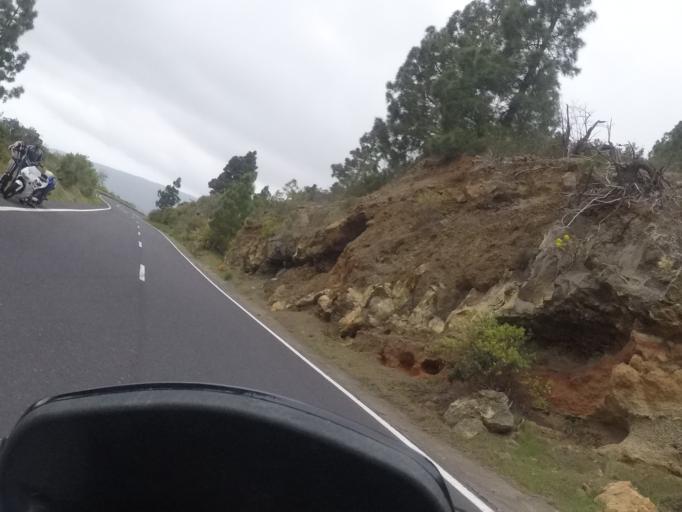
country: ES
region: Canary Islands
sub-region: Provincia de Santa Cruz de Tenerife
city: Arafo
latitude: 28.3575
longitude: -16.4273
